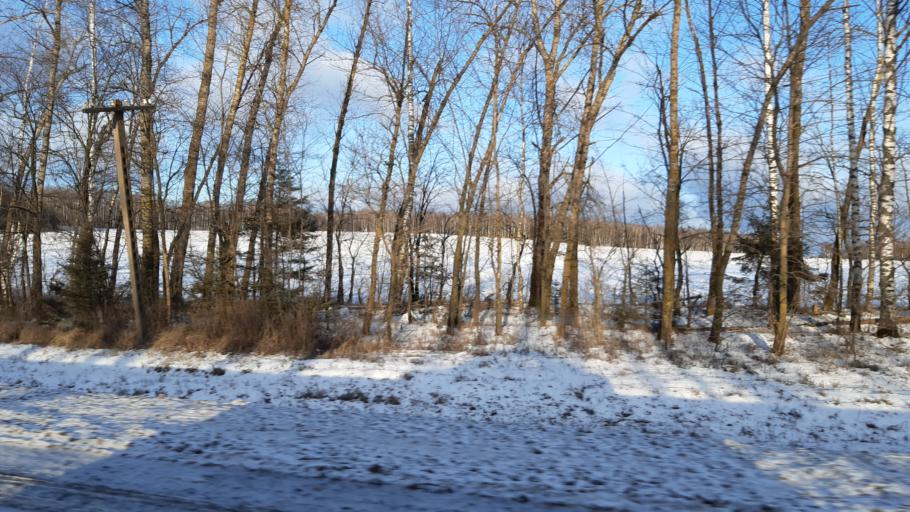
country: RU
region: Vladimir
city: Arsaki
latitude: 56.2899
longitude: 38.3850
